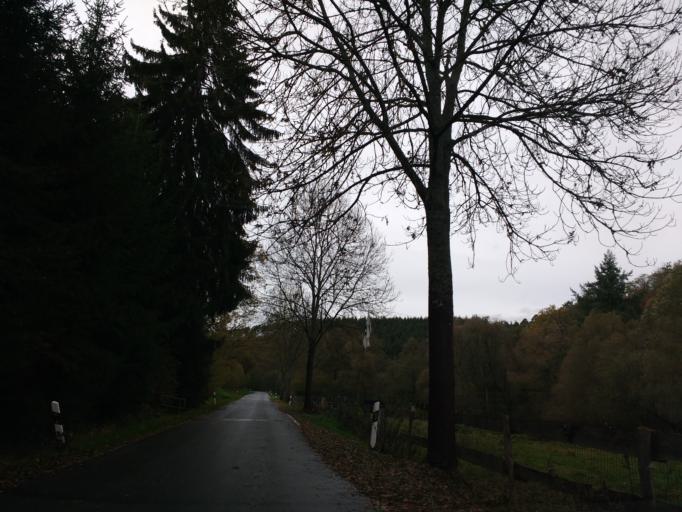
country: DE
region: Hesse
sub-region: Regierungsbezirk Kassel
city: Vohl
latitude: 51.1967
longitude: 8.9490
